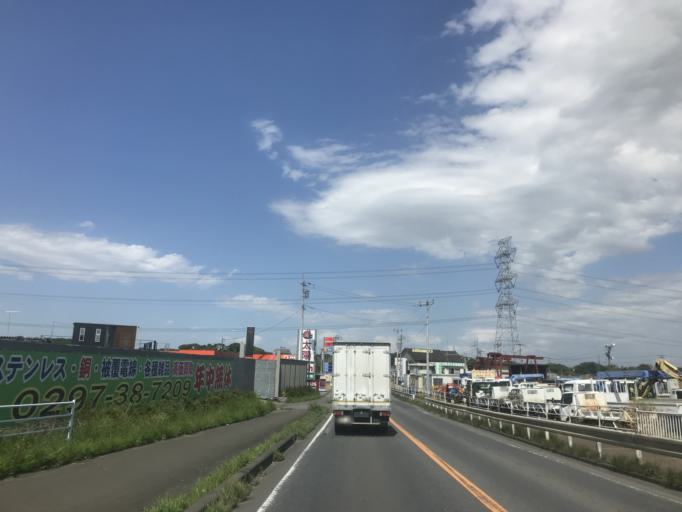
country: JP
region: Chiba
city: Noda
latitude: 35.9870
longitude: 139.8957
